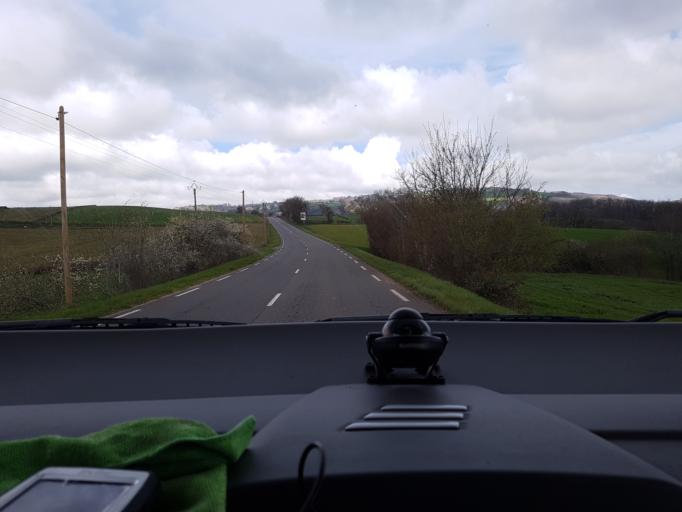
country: FR
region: Midi-Pyrenees
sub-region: Departement de l'Aveyron
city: Moyrazes
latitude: 44.3873
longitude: 2.3998
